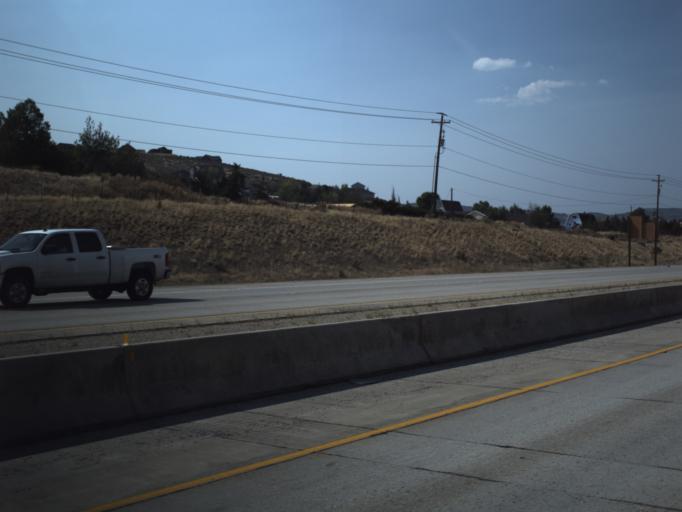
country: US
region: Utah
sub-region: Summit County
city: Snyderville
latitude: 40.7219
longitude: -111.4901
